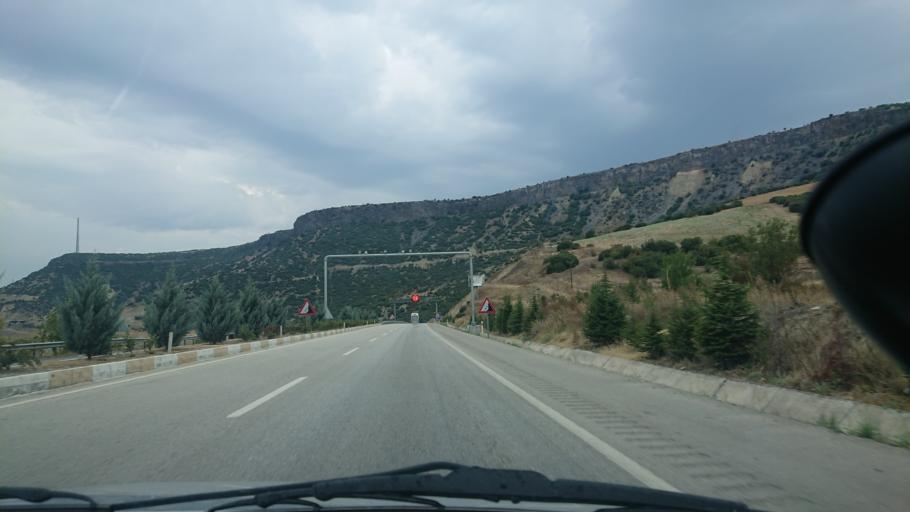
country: TR
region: Manisa
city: Selendi
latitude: 38.6170
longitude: 28.8326
